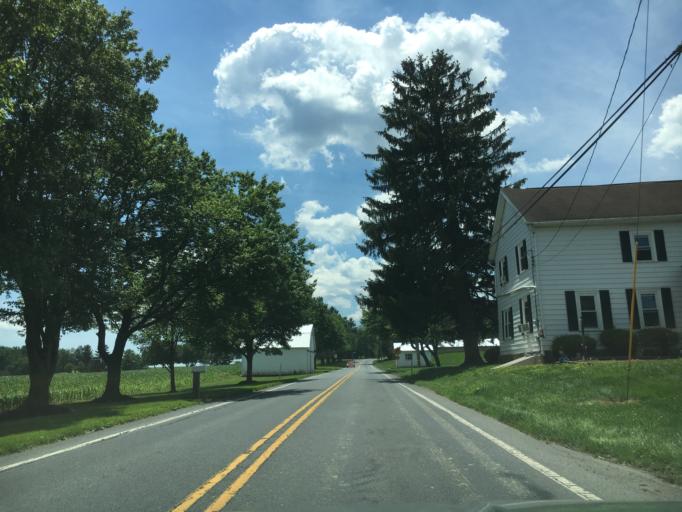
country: US
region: Pennsylvania
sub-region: Lehigh County
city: Schnecksville
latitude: 40.6550
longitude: -75.5761
